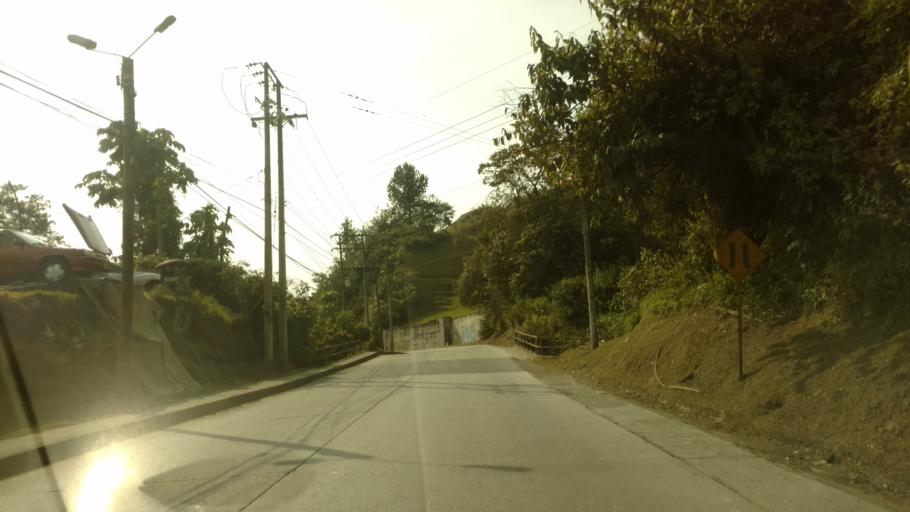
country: CO
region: Caldas
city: Manizales
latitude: 5.0727
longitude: -75.5027
